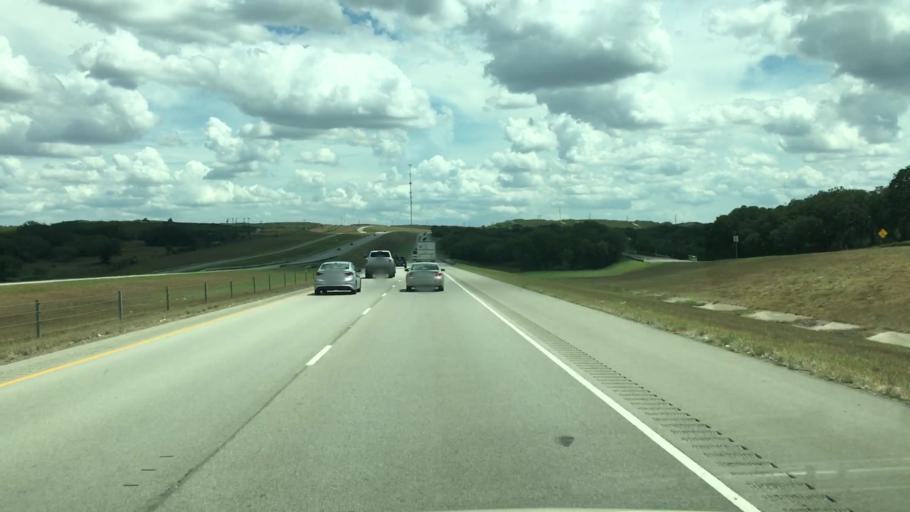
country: US
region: Texas
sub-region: Live Oak County
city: George West
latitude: 28.2631
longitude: -97.9328
